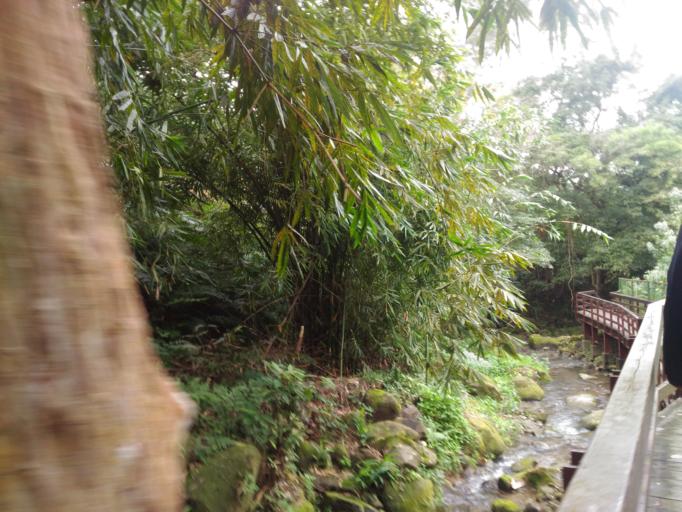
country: TW
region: Taipei
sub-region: Taipei
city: Banqiao
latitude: 24.9498
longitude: 121.4488
